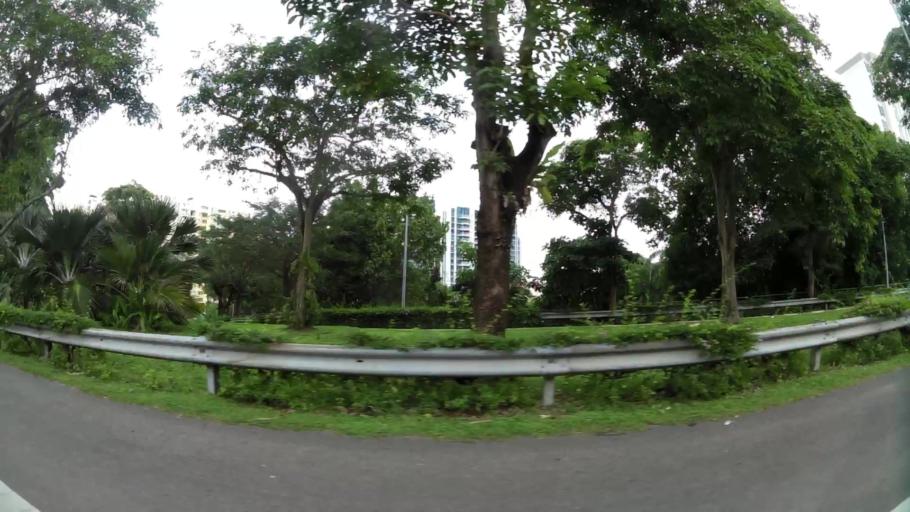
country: MY
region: Johor
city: Kampung Pasir Gudang Baru
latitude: 1.3717
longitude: 103.9403
